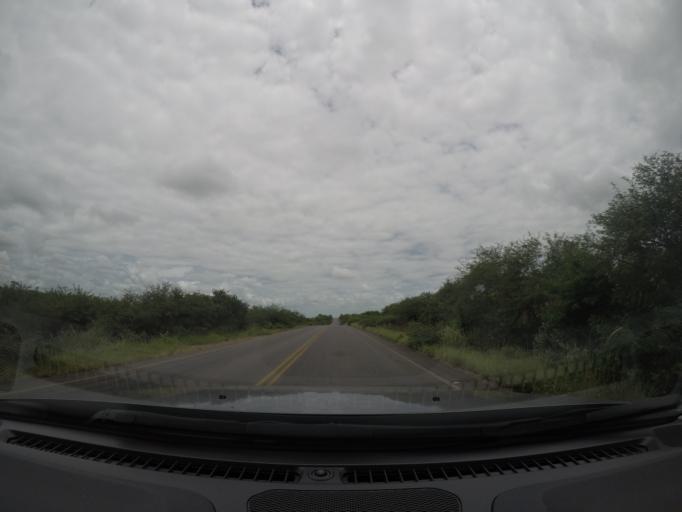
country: BR
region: Bahia
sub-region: Itaberaba
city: Itaberaba
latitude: -12.4985
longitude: -40.2425
